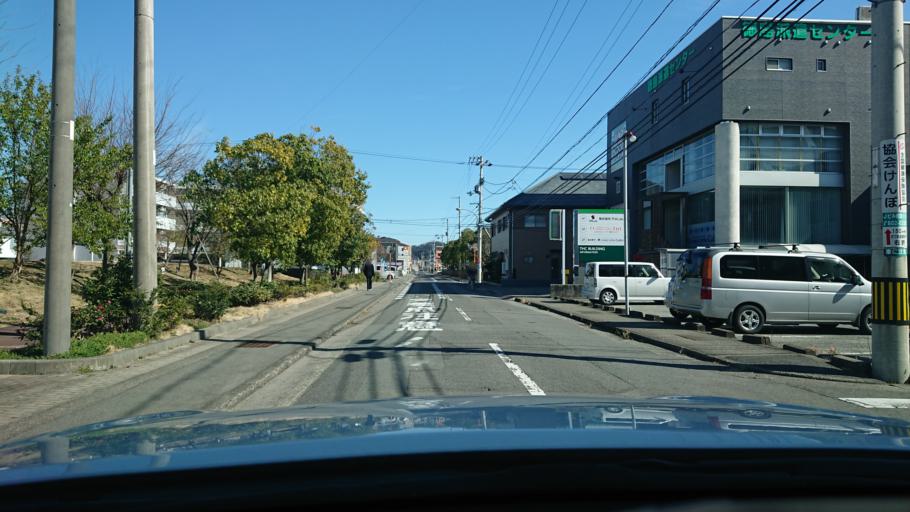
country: JP
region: Tokushima
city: Tokushima-shi
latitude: 34.0516
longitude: 134.5538
